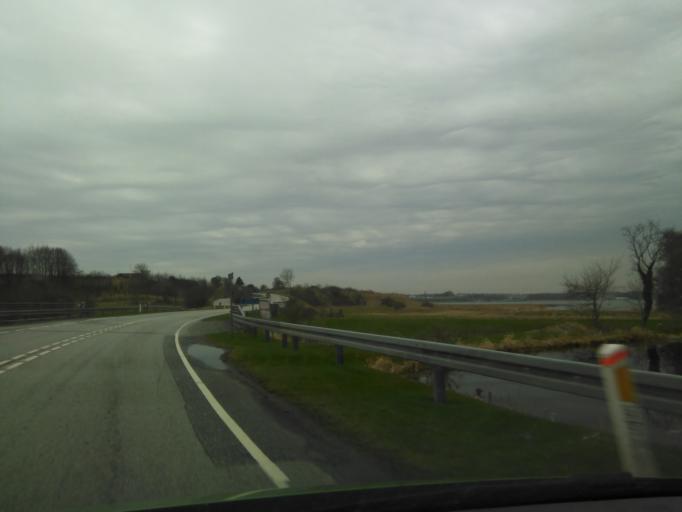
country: DK
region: North Denmark
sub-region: Mariagerfjord Kommune
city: Hadsund
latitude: 56.6889
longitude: 10.1030
